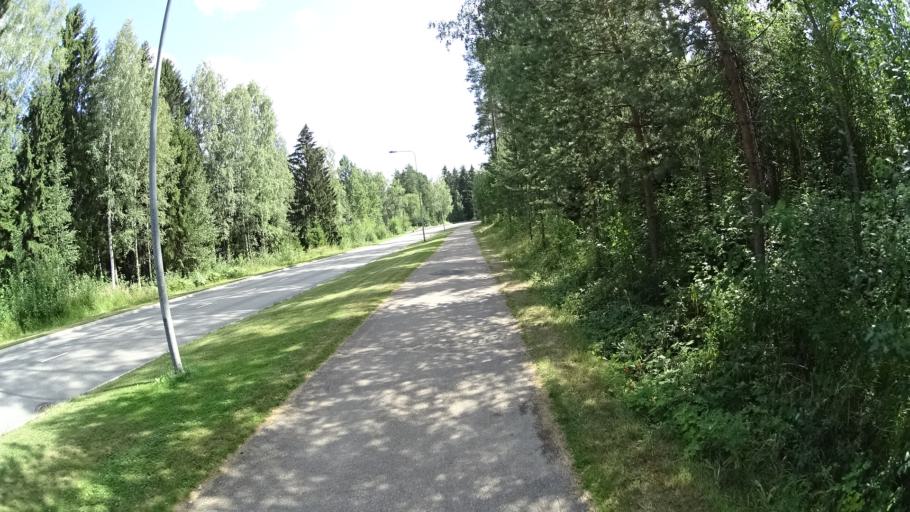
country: FI
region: Uusimaa
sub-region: Porvoo
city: Porvoo
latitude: 60.3915
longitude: 25.7061
